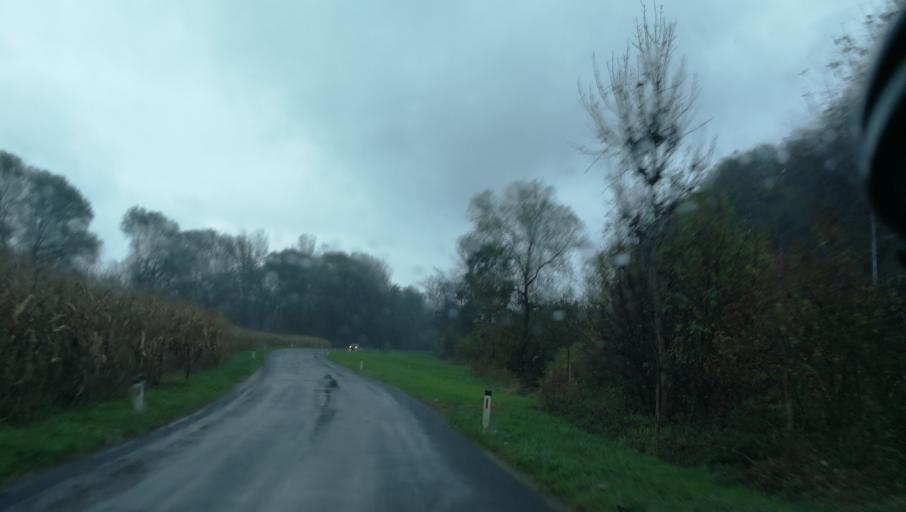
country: AT
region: Styria
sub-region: Politischer Bezirk Leibnitz
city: Strass in Steiermark
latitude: 46.7145
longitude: 15.6207
